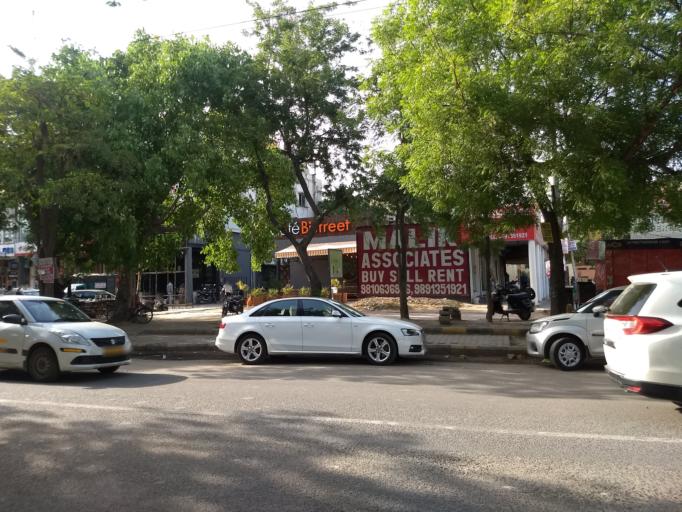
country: IN
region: Haryana
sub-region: Gurgaon
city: Gurgaon
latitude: 28.5026
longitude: 77.0641
